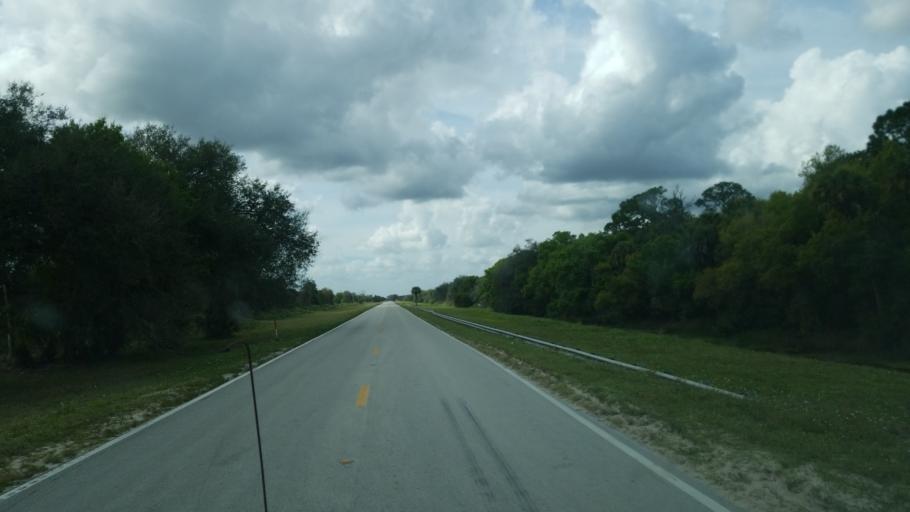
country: US
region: Florida
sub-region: Indian River County
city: West Vero Corridor
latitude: 27.4484
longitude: -80.6459
